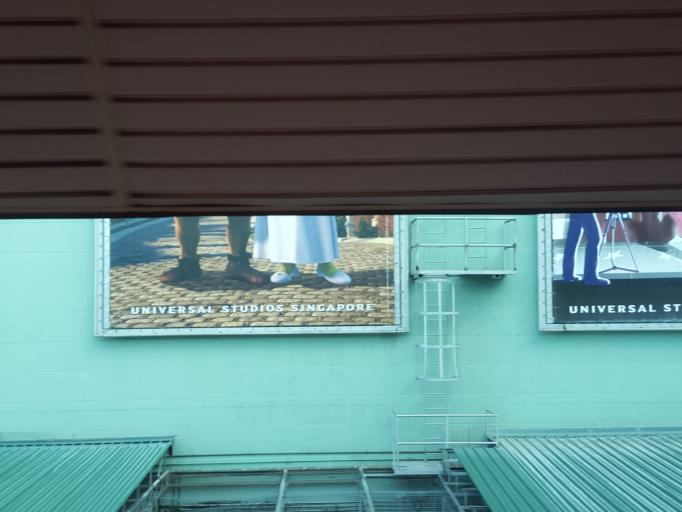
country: SG
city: Singapore
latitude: 1.2556
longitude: 103.8211
